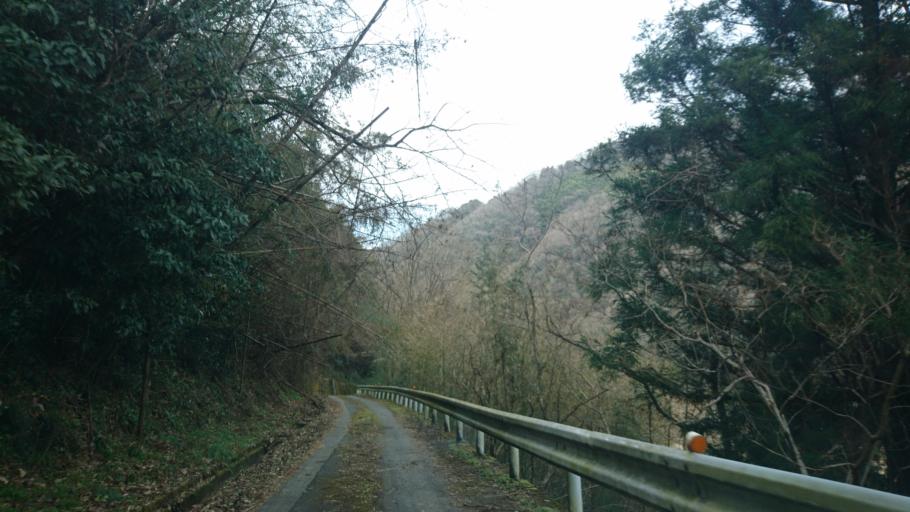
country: JP
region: Okayama
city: Takahashi
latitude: 34.8742
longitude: 133.5604
